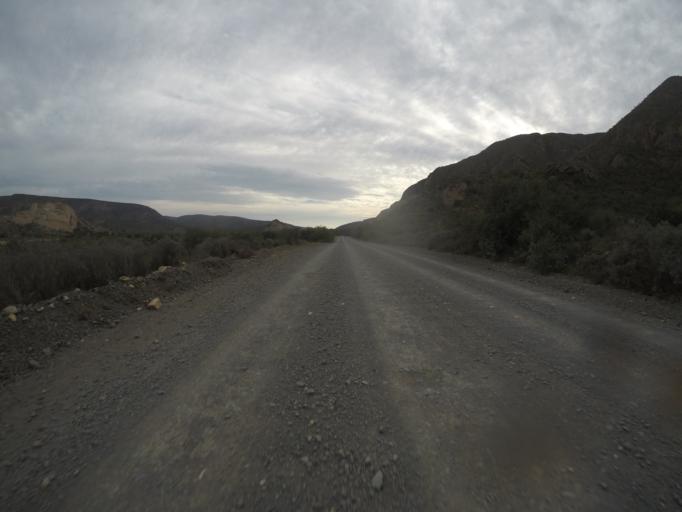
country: ZA
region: Eastern Cape
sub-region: Cacadu District Municipality
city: Willowmore
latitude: -33.5192
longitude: 23.6888
